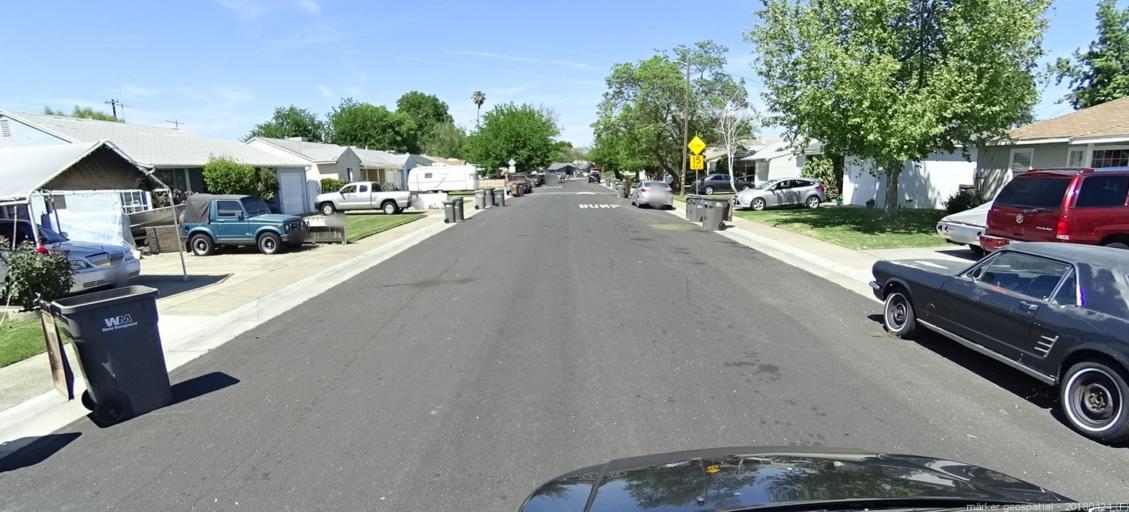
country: US
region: California
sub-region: Yolo County
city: West Sacramento
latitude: 38.5851
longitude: -121.5337
